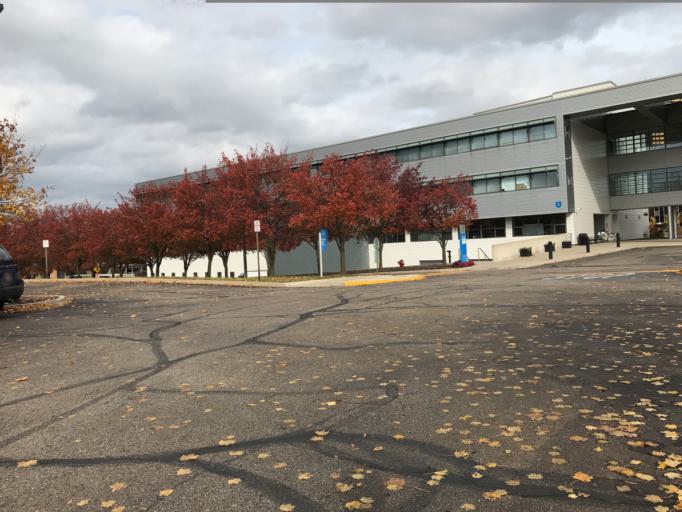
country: US
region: Michigan
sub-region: Oakland County
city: Southfield
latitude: 42.4736
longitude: -83.2504
